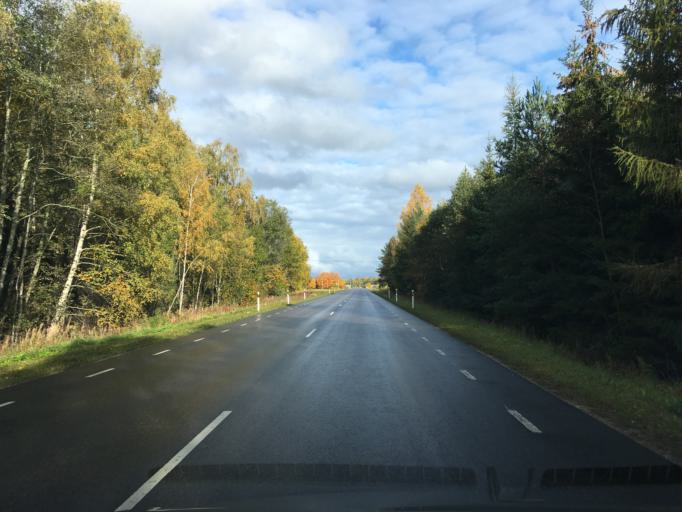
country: EE
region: Harju
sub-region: Raasiku vald
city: Raasiku
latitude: 59.1968
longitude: 25.1847
